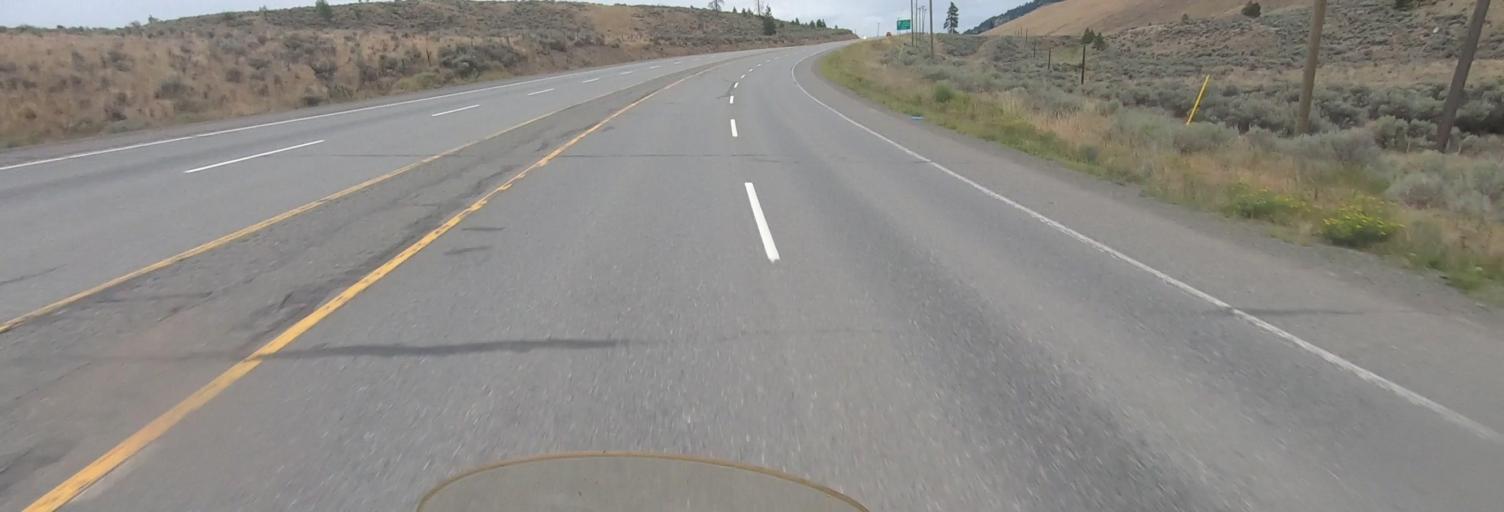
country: CA
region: British Columbia
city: Kamloops
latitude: 50.6701
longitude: -120.4838
